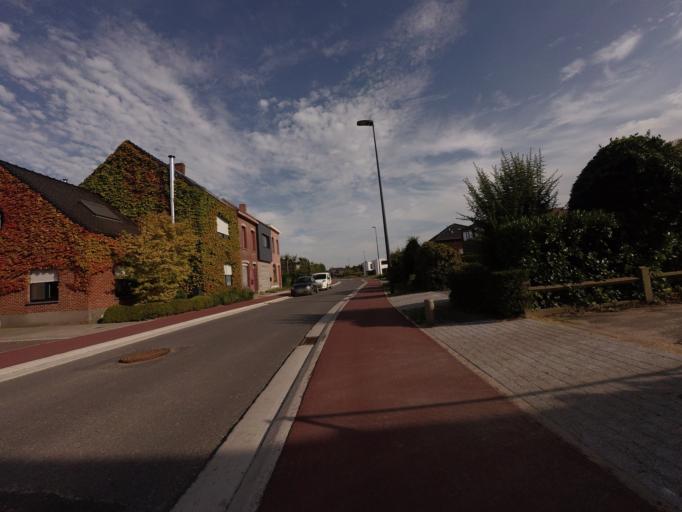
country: BE
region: Flanders
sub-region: Provincie Vlaams-Brabant
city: Boortmeerbeek
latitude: 50.9753
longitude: 4.5737
